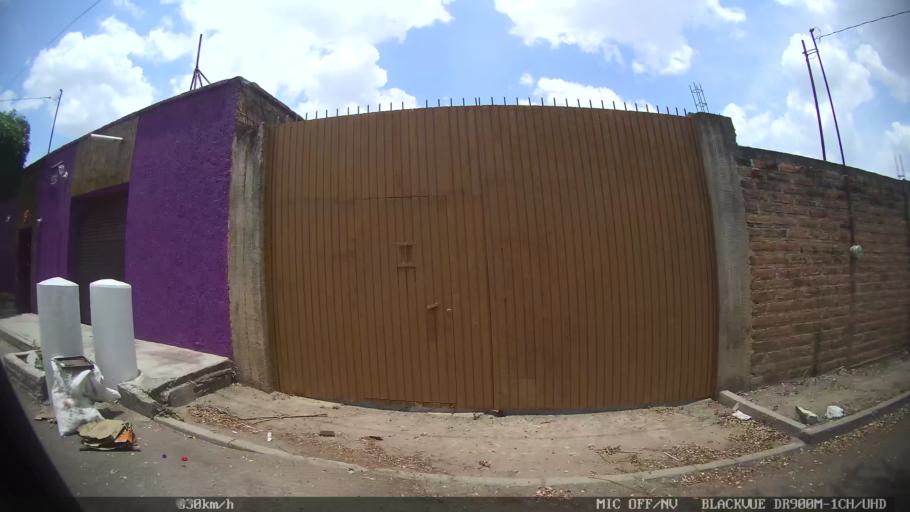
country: MX
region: Jalisco
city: Tonala
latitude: 20.6571
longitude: -103.2263
